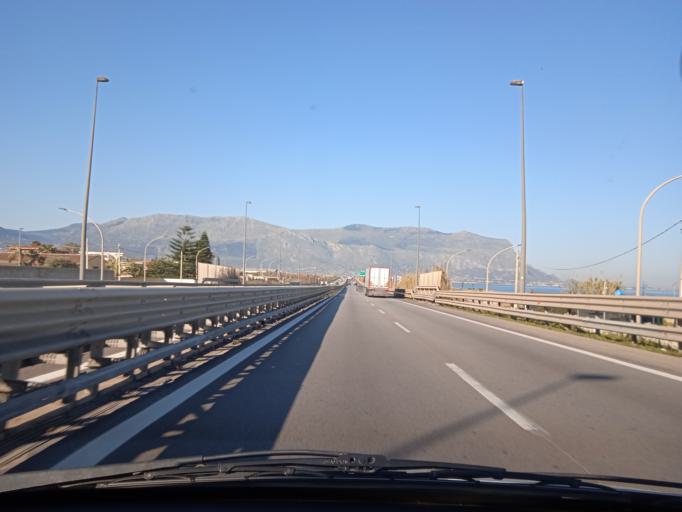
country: IT
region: Sicily
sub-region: Palermo
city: Capaci
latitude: 38.1809
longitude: 13.2314
